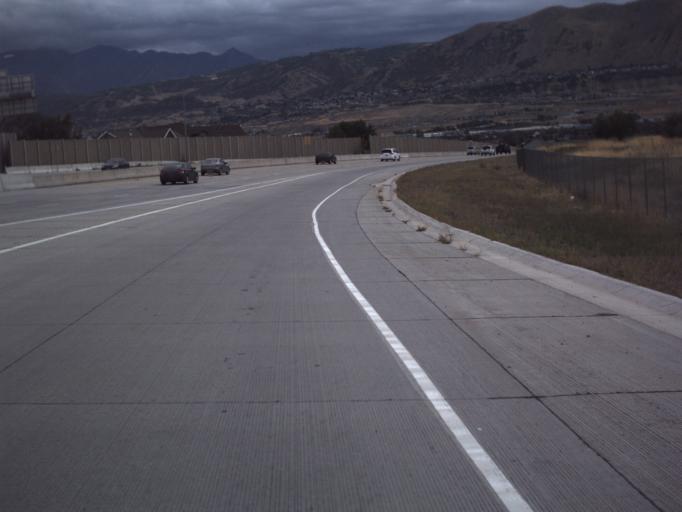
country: US
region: Utah
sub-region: Salt Lake County
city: Bluffdale
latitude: 40.5000
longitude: -111.9351
